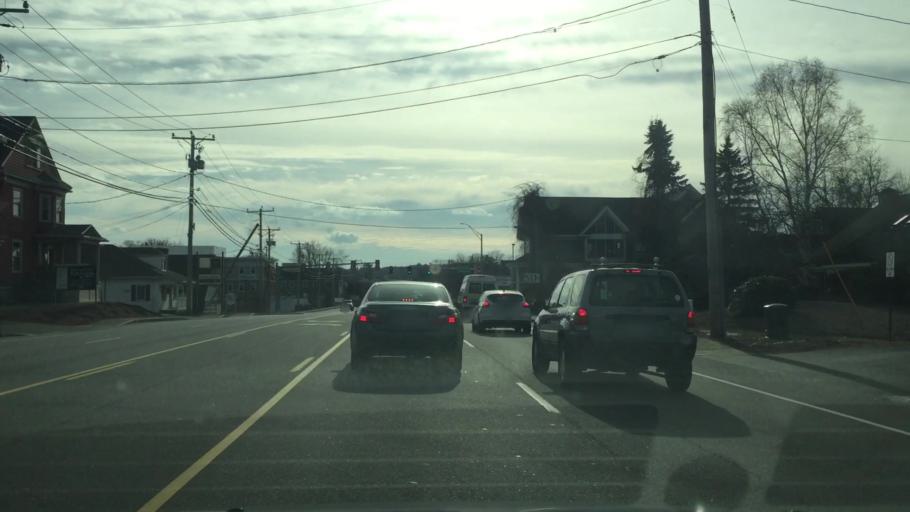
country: US
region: New Hampshire
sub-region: Hillsborough County
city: Bedford
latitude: 42.9624
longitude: -71.4800
